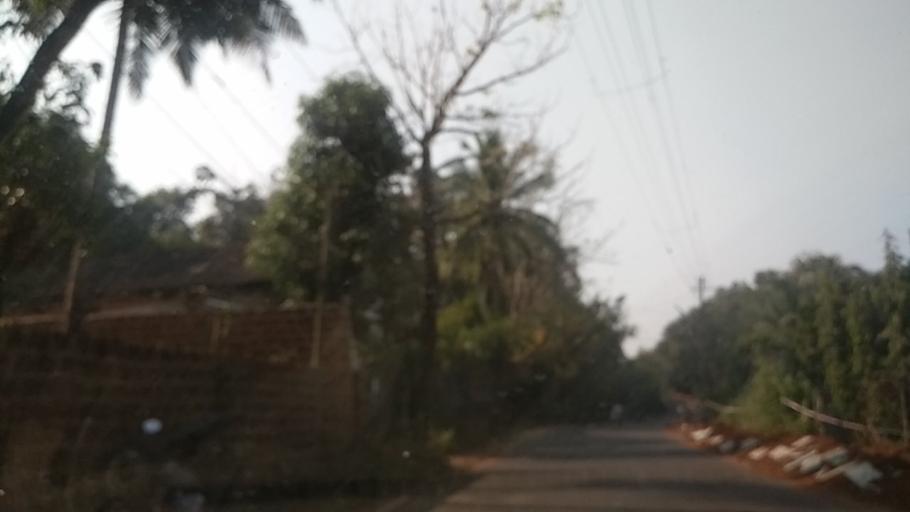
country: IN
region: Goa
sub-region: North Goa
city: Pernem
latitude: 15.7148
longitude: 73.8060
